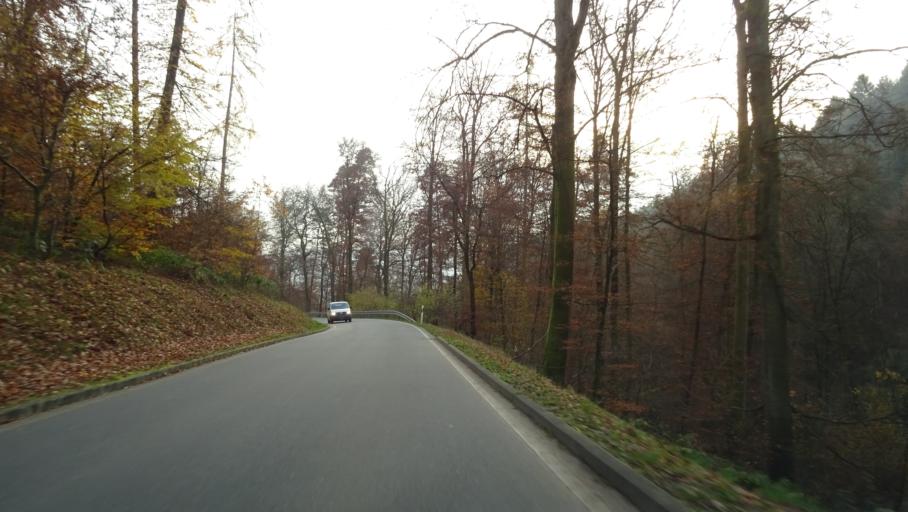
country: DE
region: Baden-Wuerttemberg
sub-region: Karlsruhe Region
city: Neckargerach
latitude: 49.4115
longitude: 9.0791
